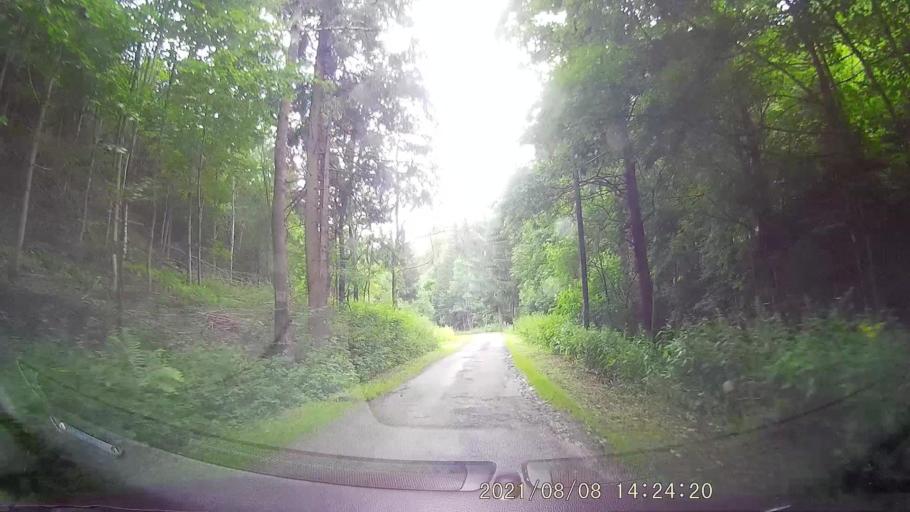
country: PL
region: Lower Silesian Voivodeship
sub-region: Powiat klodzki
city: Lewin Klodzki
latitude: 50.4407
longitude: 16.2994
